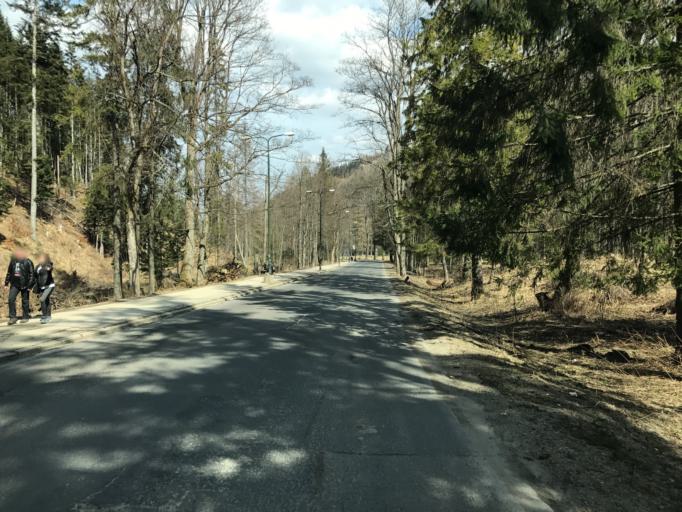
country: PL
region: Lesser Poland Voivodeship
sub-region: Powiat tatrzanski
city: Zakopane
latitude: 49.2714
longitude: 19.9801
